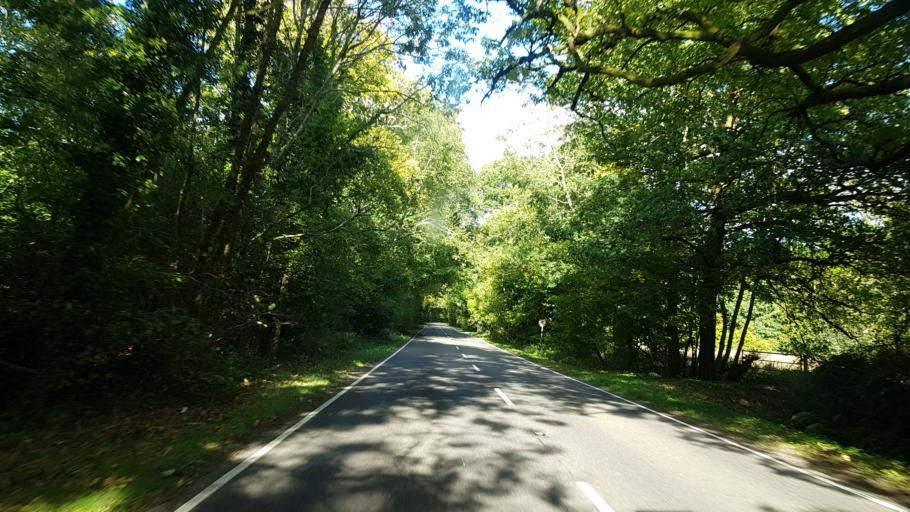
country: GB
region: England
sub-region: Surrey
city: Chiddingfold
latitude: 51.0917
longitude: -0.6432
